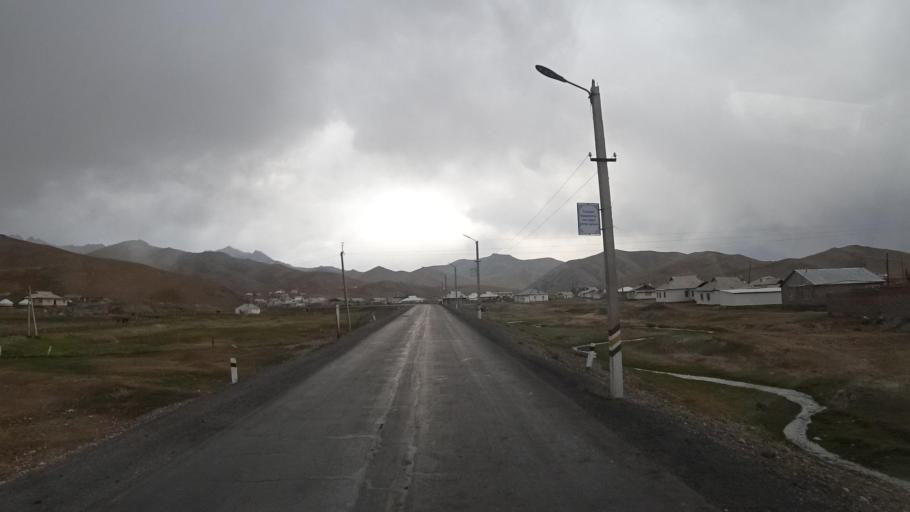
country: KG
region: Osh
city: Gul'cha
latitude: 39.7215
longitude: 73.2467
